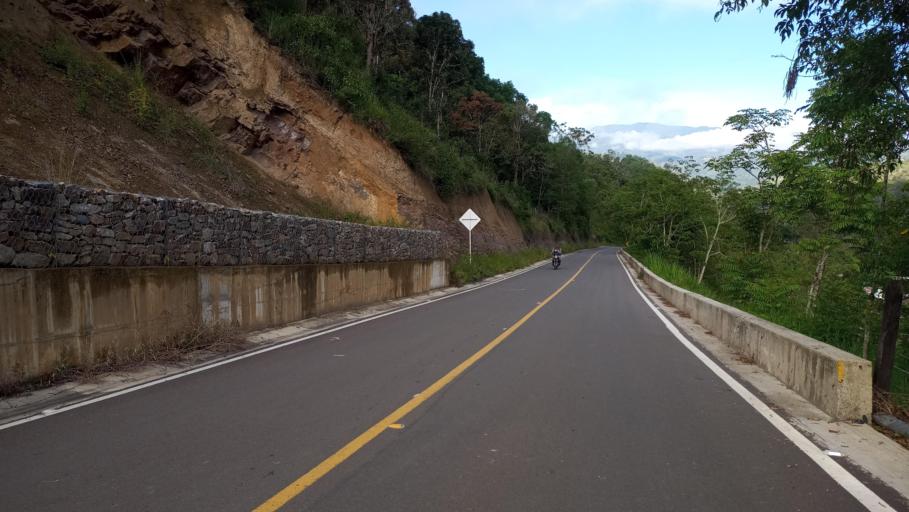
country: CO
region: Boyaca
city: Somondoco
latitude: 5.0058
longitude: -73.4296
